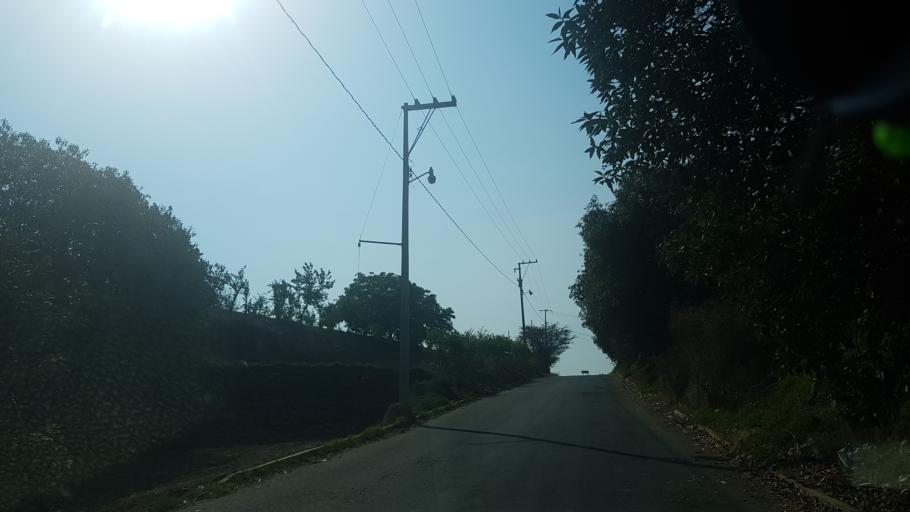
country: MX
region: Puebla
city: San Nicolas de los Ranchos
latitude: 19.0715
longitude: -98.4771
